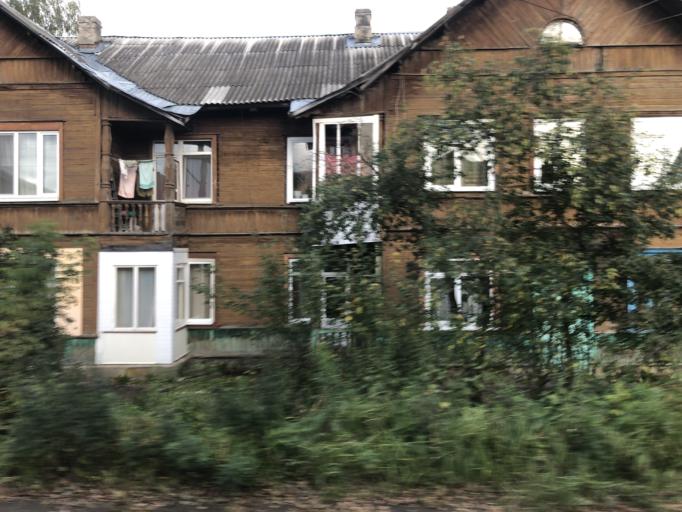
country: RU
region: Tverskaya
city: Rzhev
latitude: 56.2535
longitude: 34.2930
